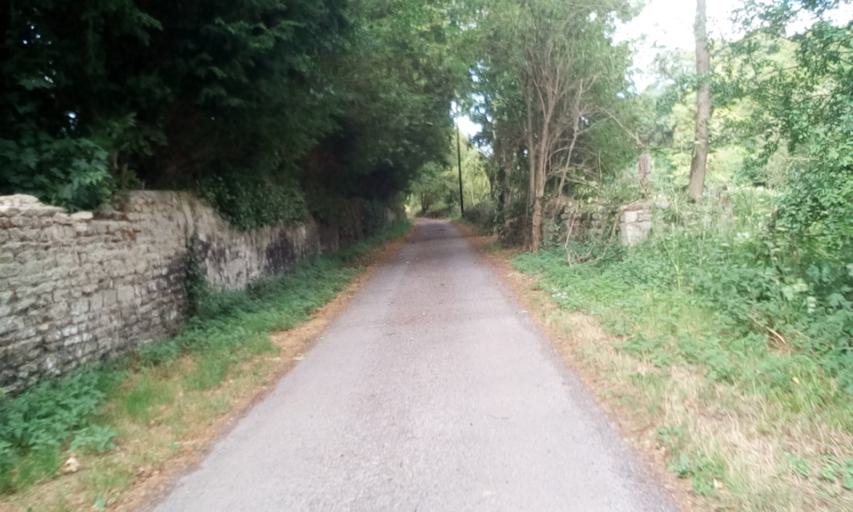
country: FR
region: Lower Normandy
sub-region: Departement du Calvados
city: Creully
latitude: 49.2899
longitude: -0.5116
